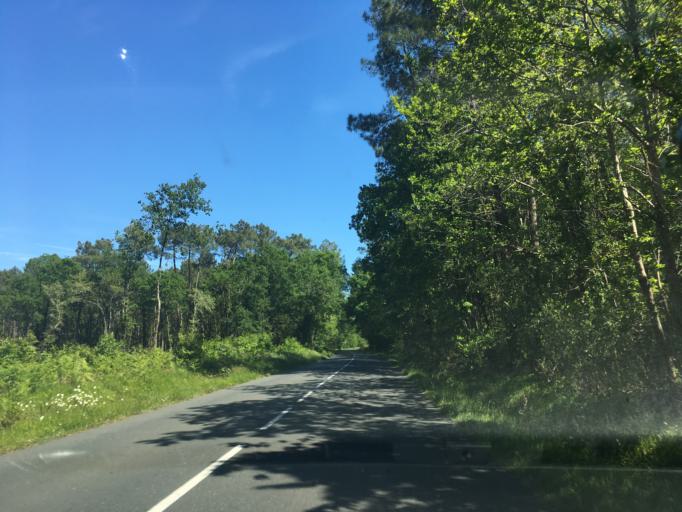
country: FR
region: Aquitaine
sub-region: Departement de la Gironde
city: Lesparre-Medoc
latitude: 45.2855
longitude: -0.8971
